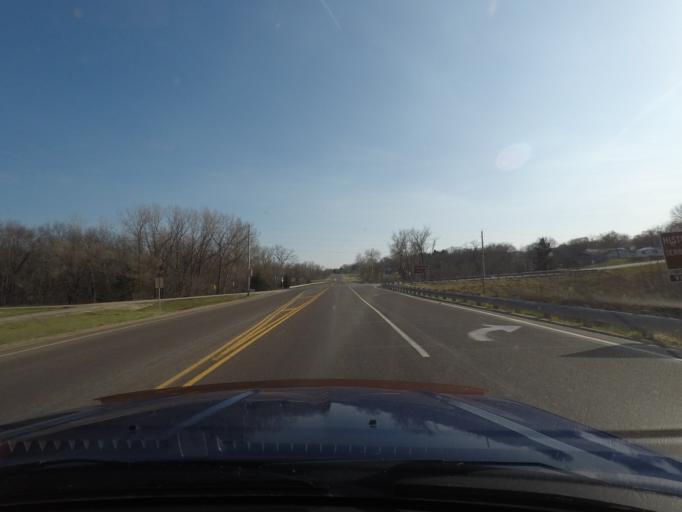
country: US
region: Kansas
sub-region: Douglas County
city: Lawrence
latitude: 39.0448
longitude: -95.3900
